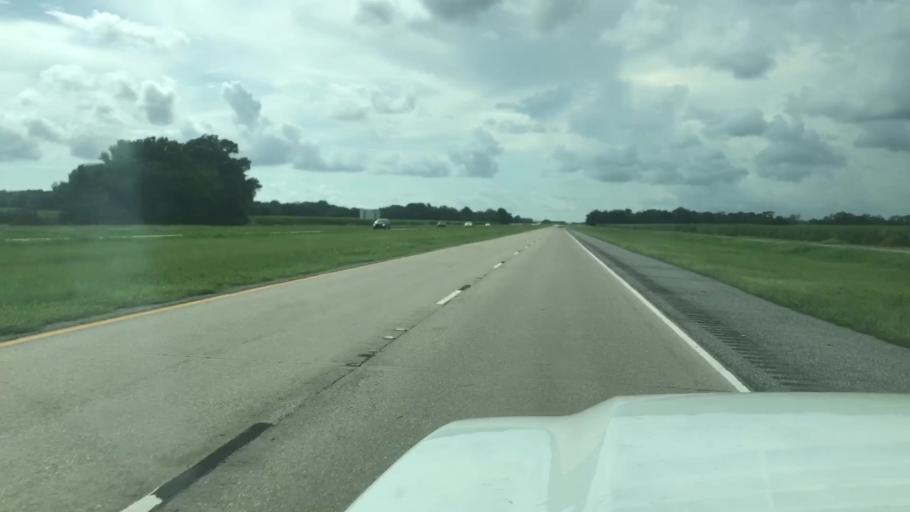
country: US
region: Louisiana
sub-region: Saint Mary Parish
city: Franklin
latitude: 29.7605
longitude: -91.4781
